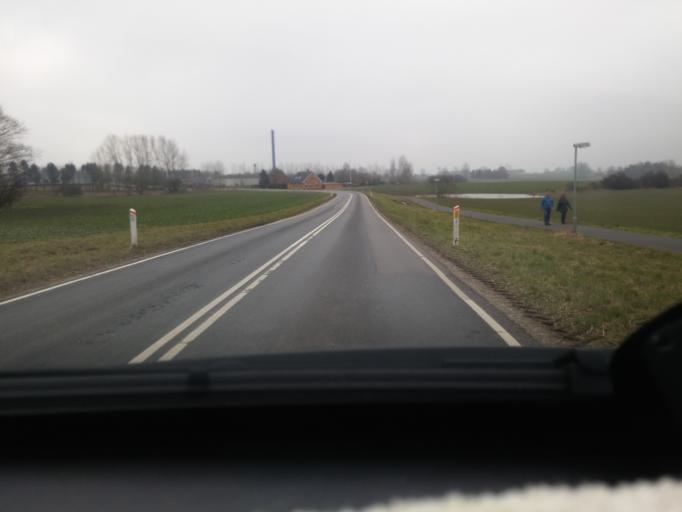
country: DK
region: South Denmark
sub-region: Nyborg Kommune
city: Ullerslev
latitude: 55.3675
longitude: 10.7258
